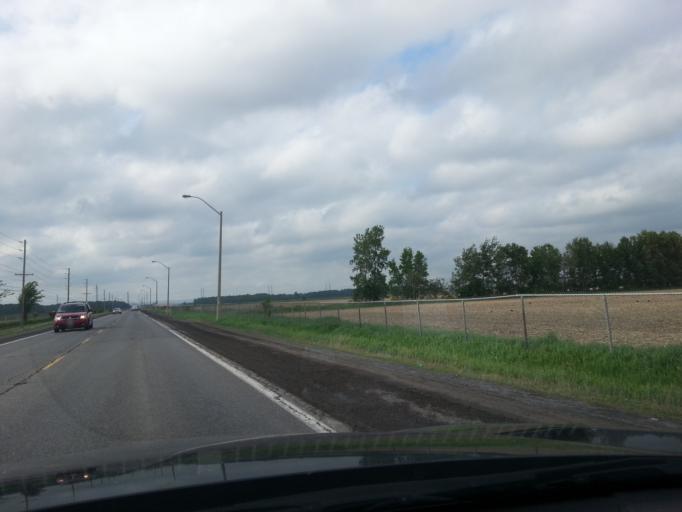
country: CA
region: Ontario
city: Bells Corners
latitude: 45.2997
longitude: -75.7639
